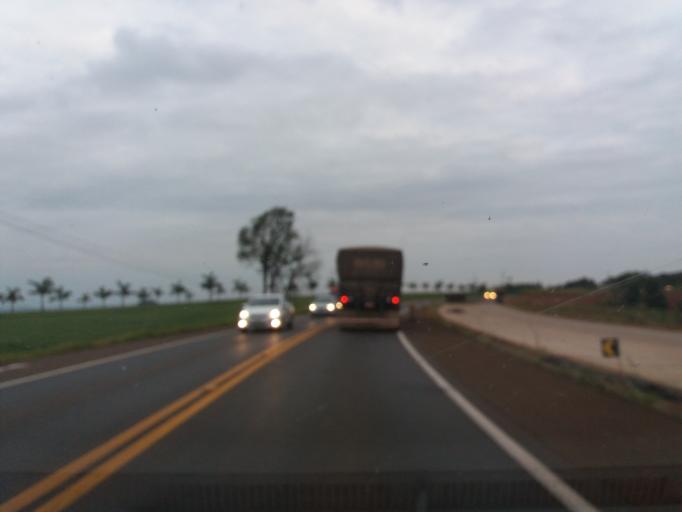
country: BR
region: Parana
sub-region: Cascavel
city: Cascavel
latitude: -25.2443
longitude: -53.5796
